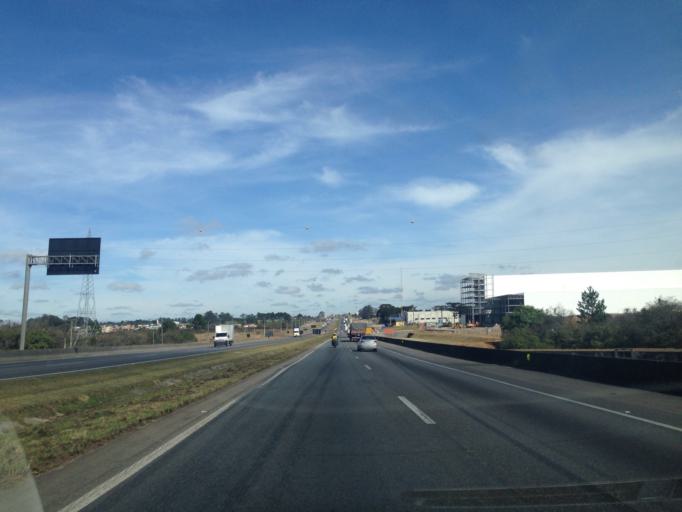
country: BR
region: Parana
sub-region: Sao Jose Dos Pinhais
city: Sao Jose dos Pinhais
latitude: -25.5239
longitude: -49.1377
